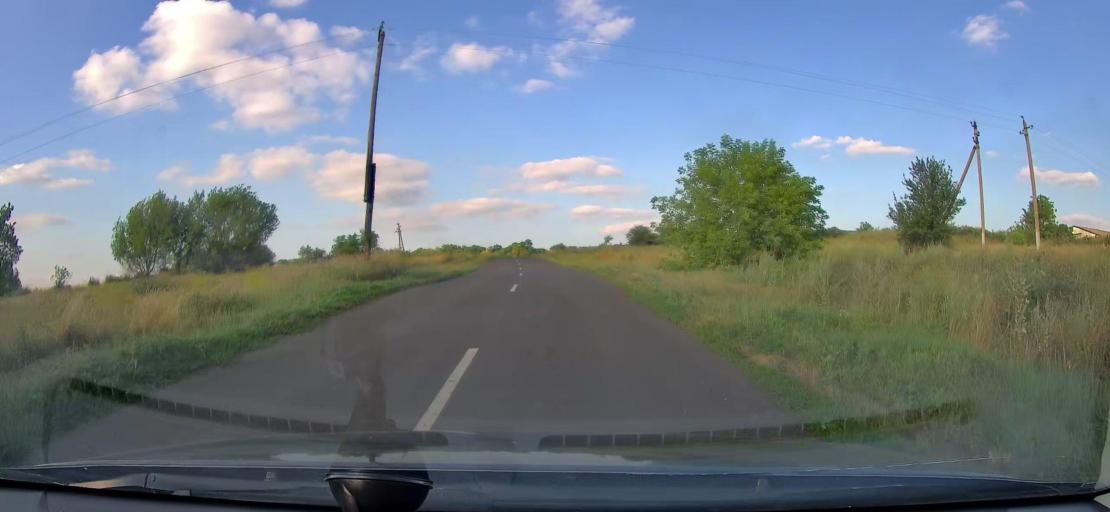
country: RU
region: Kursk
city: Zolotukhino
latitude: 52.0262
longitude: 36.2091
